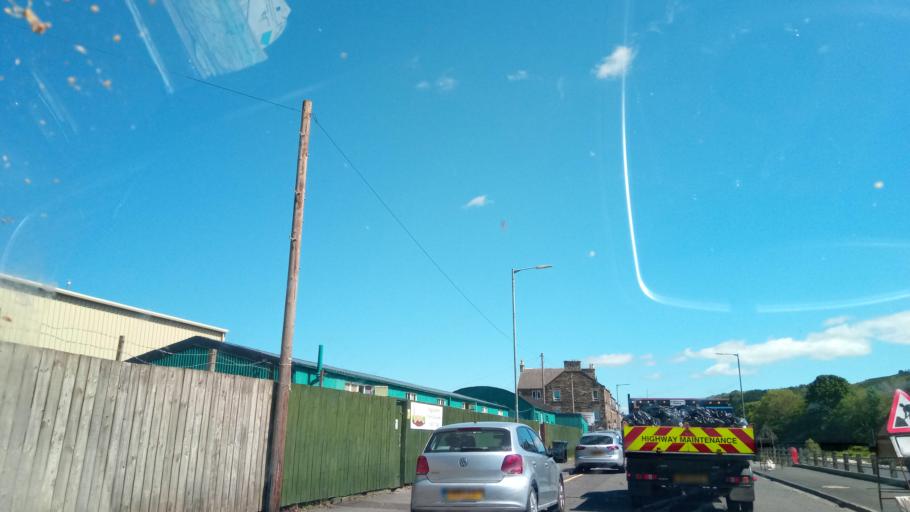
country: GB
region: Scotland
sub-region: The Scottish Borders
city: Hawick
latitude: 55.4292
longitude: -2.7787
